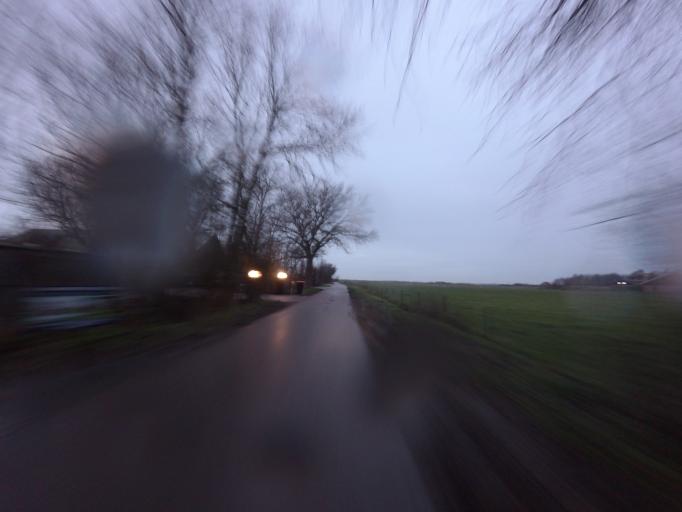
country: NL
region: North Holland
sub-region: Gemeente Texel
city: Den Burg
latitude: 53.0651
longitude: 4.8022
